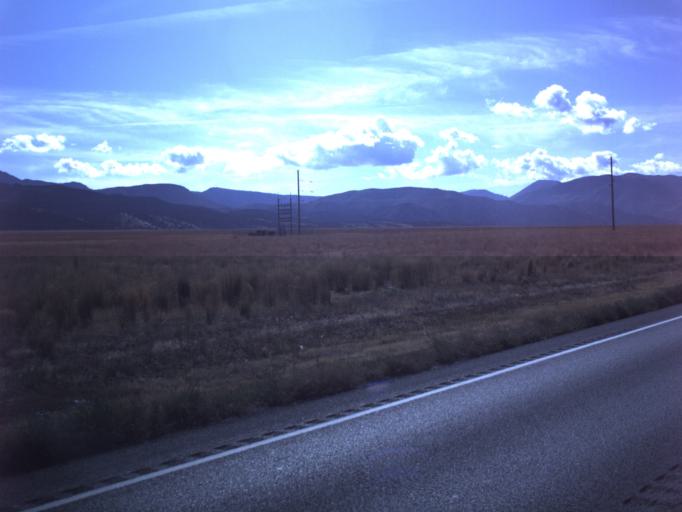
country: US
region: Utah
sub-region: Juab County
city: Nephi
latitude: 39.6333
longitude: -111.8616
